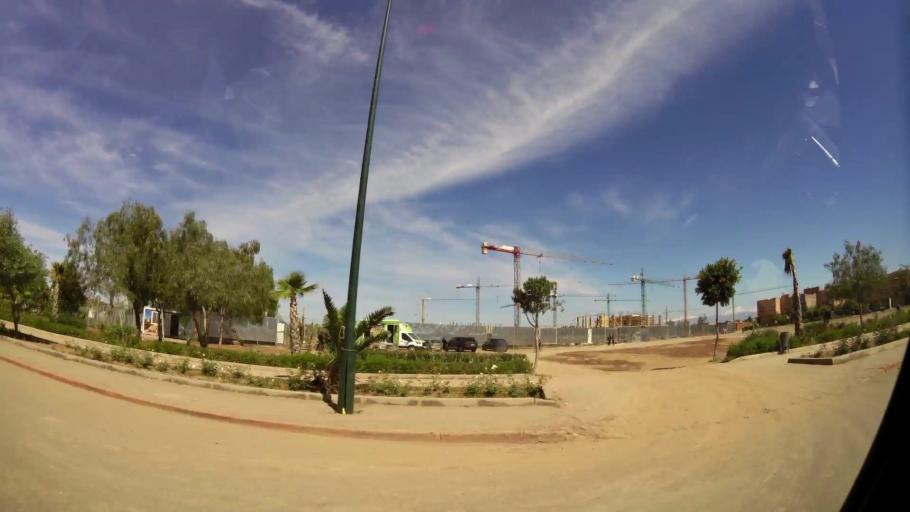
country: MA
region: Marrakech-Tensift-Al Haouz
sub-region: Marrakech
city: Marrakesh
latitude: 31.6028
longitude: -7.9614
